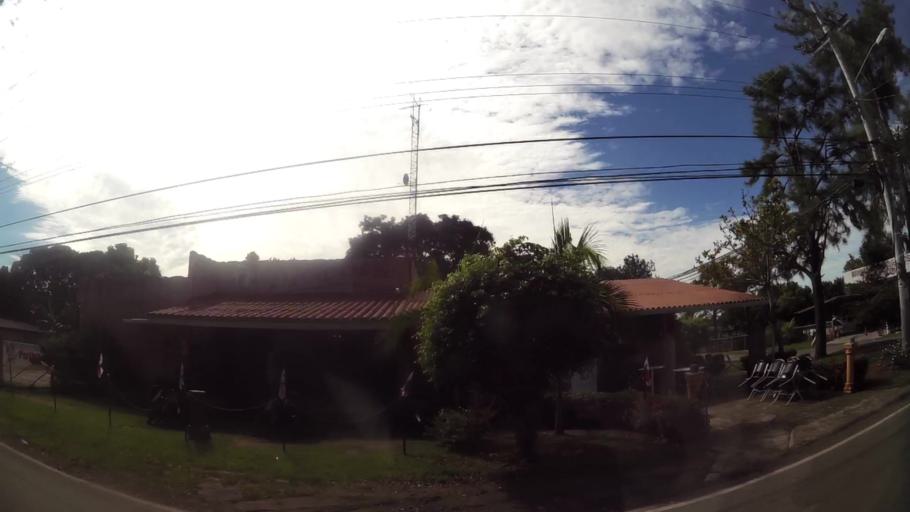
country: PA
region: Panama
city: Nueva Gorgona
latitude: 8.5303
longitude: -79.8936
